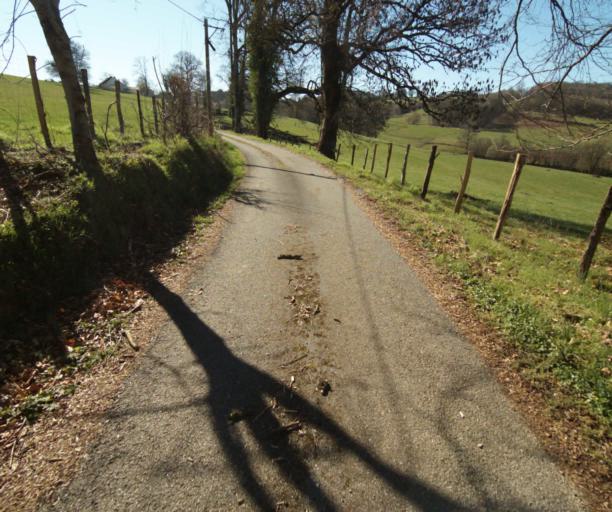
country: FR
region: Limousin
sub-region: Departement de la Correze
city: Chamboulive
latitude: 45.4028
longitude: 1.6981
